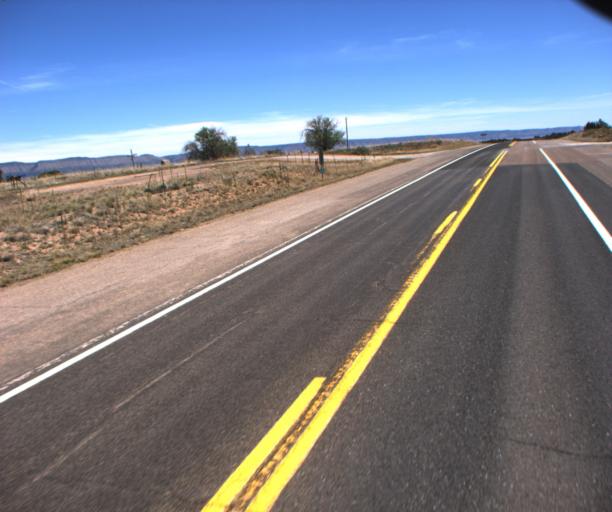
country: US
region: Arizona
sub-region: Mohave County
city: Peach Springs
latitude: 35.5204
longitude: -113.2056
